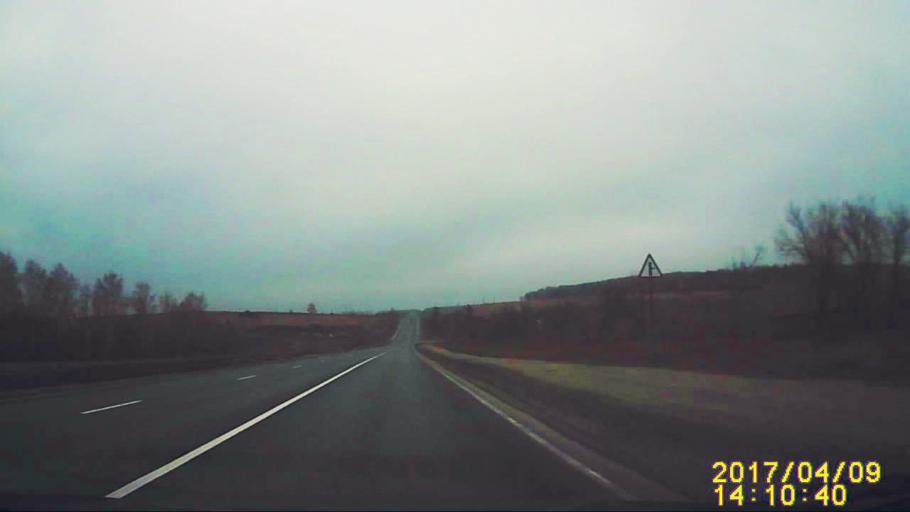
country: RU
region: Ulyanovsk
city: Krasnyy Gulyay
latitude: 54.0406
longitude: 48.2139
